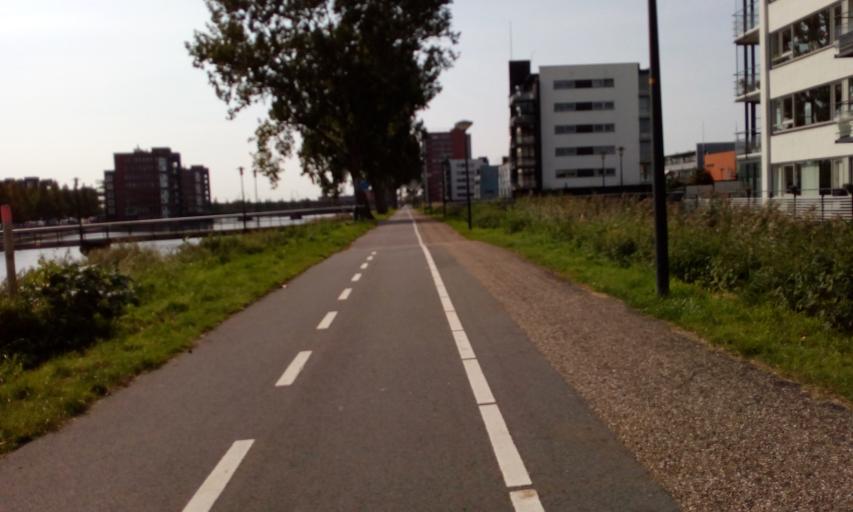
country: NL
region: South Holland
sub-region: Gemeente Rijswijk
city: Rijswijk
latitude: 52.0257
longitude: 4.2961
